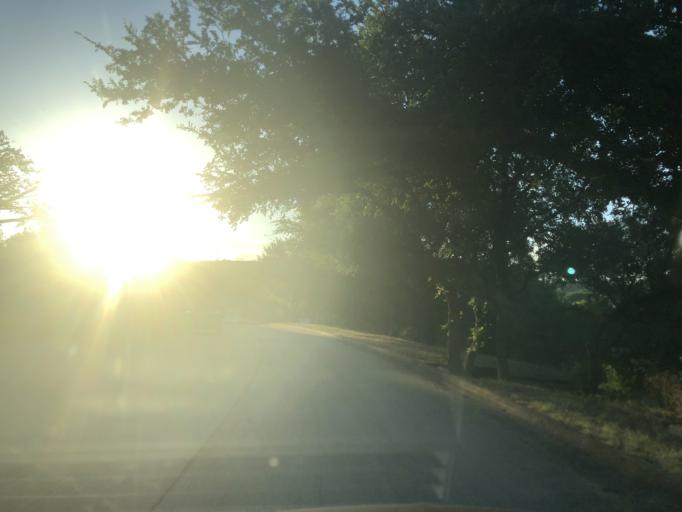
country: US
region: Texas
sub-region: Dallas County
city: Cedar Hill
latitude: 32.6484
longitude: -96.9697
